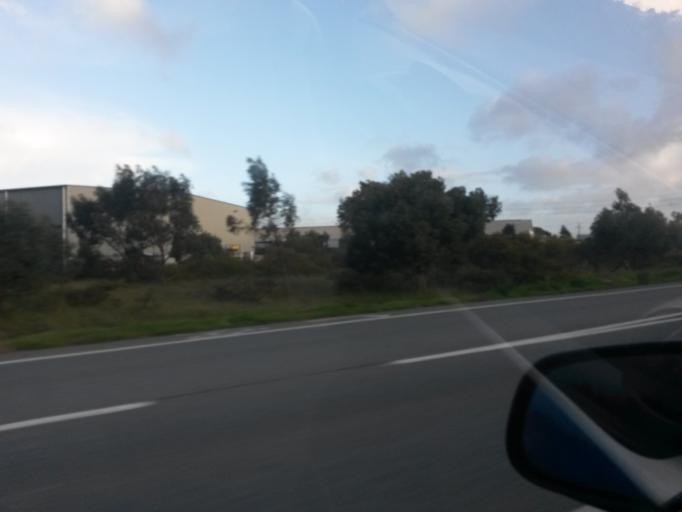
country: AU
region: South Australia
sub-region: Port Adelaide Enfield
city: Alberton
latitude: -34.8373
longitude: 138.5250
